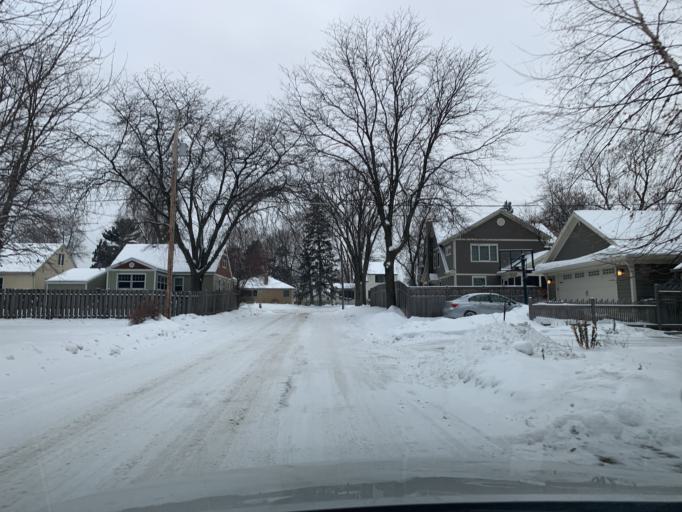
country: US
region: Minnesota
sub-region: Hennepin County
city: Saint Louis Park
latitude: 44.9298
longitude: -93.3421
